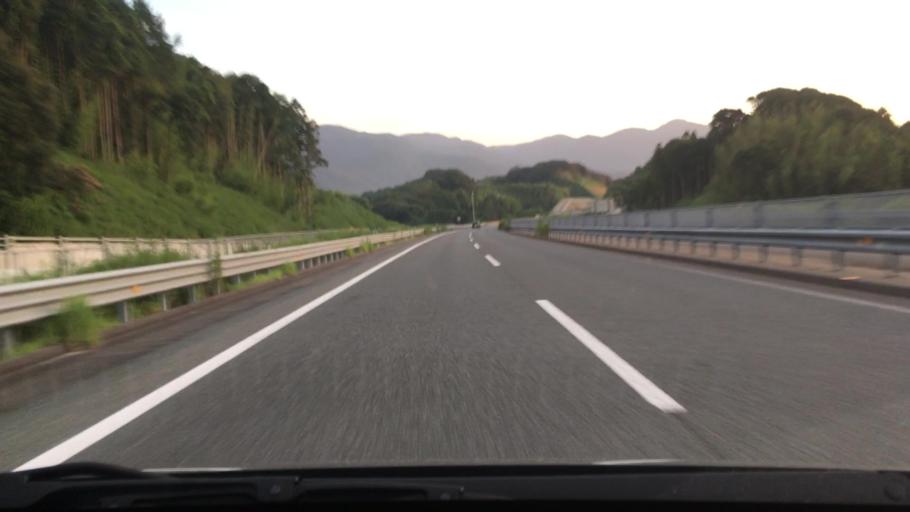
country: JP
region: Fukuoka
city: Maebaru-chuo
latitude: 33.5368
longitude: 130.1956
